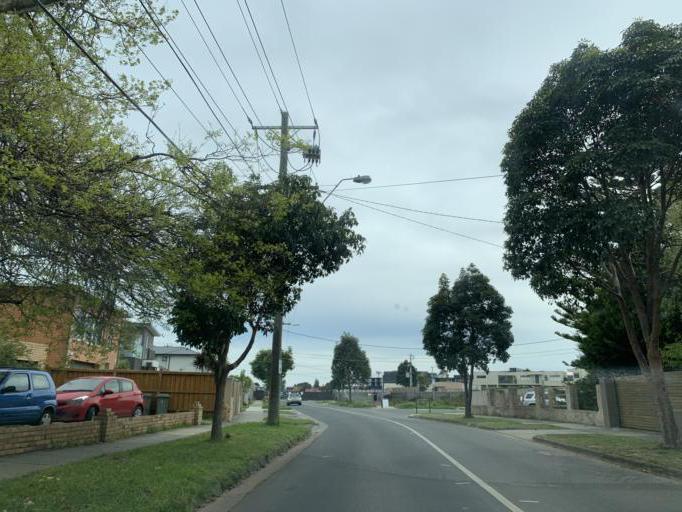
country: AU
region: Victoria
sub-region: Bayside
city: Highett
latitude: -37.9528
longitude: 145.0420
